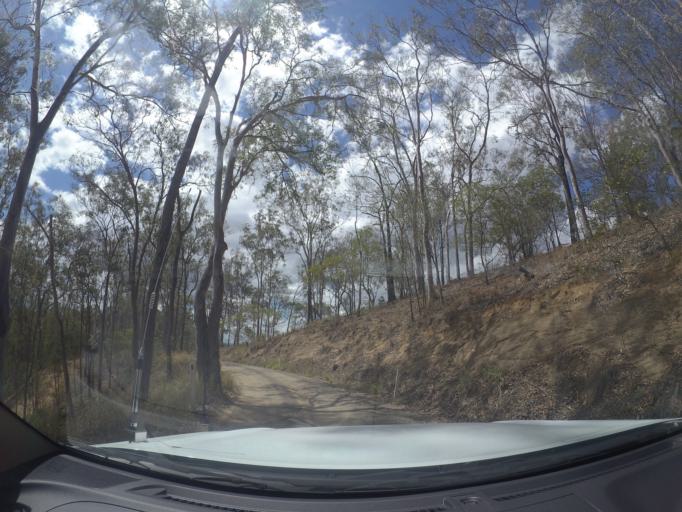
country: AU
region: Queensland
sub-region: Logan
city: Cedar Vale
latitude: -27.8949
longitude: 153.0459
